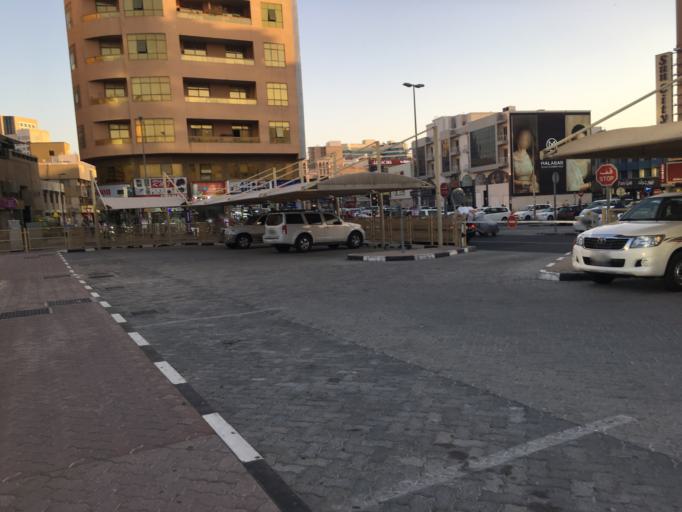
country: AE
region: Ash Shariqah
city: Sharjah
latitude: 25.2631
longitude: 55.2970
